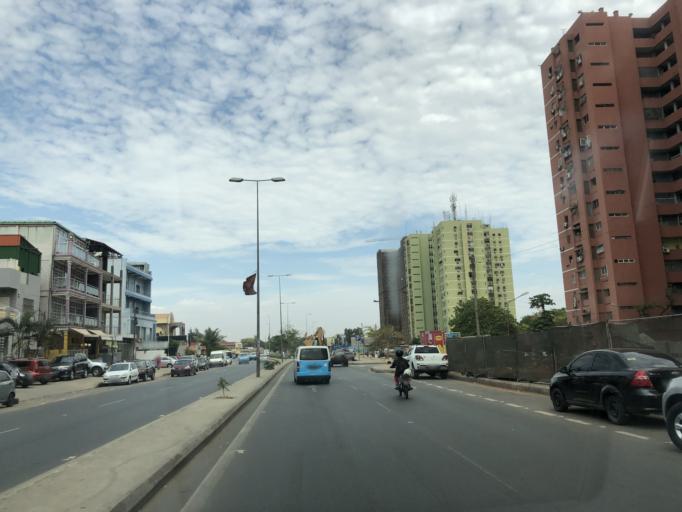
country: AO
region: Luanda
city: Luanda
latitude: -8.8245
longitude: 13.2550
